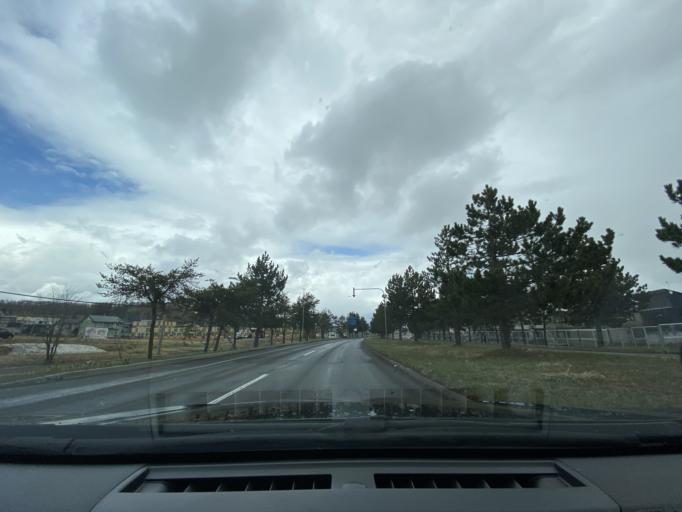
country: JP
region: Hokkaido
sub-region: Asahikawa-shi
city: Asahikawa
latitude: 43.7782
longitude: 142.3070
